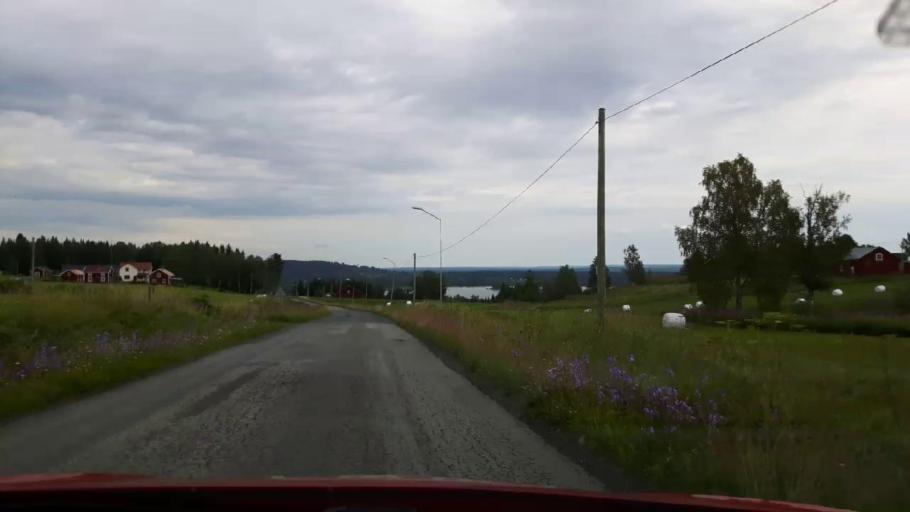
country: SE
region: Jaemtland
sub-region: Stroemsunds Kommun
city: Stroemsund
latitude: 63.5239
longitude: 15.3561
